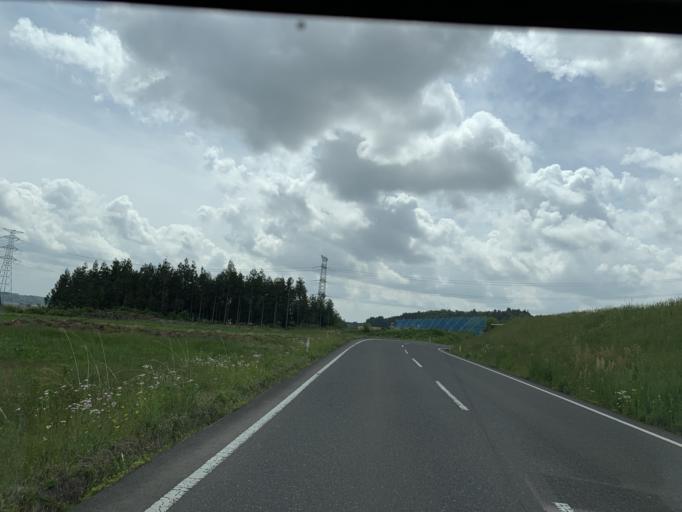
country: JP
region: Iwate
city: Ichinoseki
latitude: 38.8155
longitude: 141.0209
